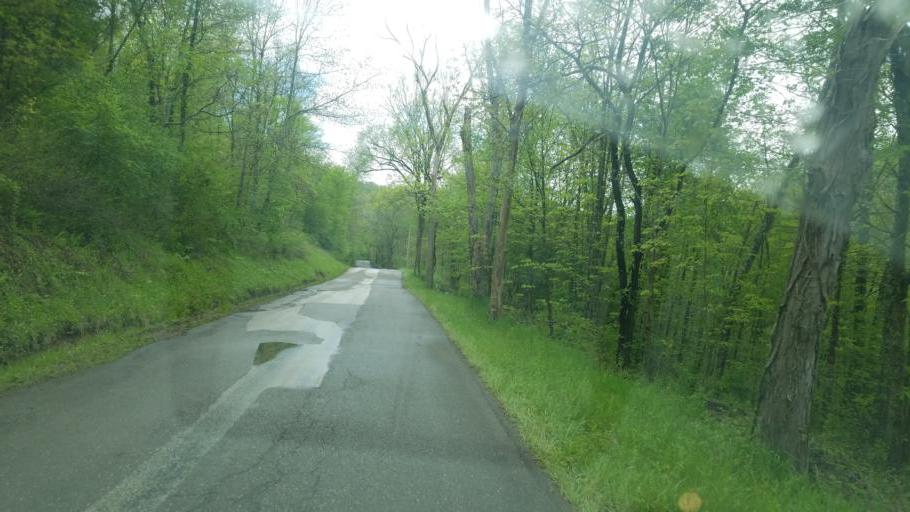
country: US
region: Ohio
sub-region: Tuscarawas County
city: Rockford
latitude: 40.4014
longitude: -81.2042
